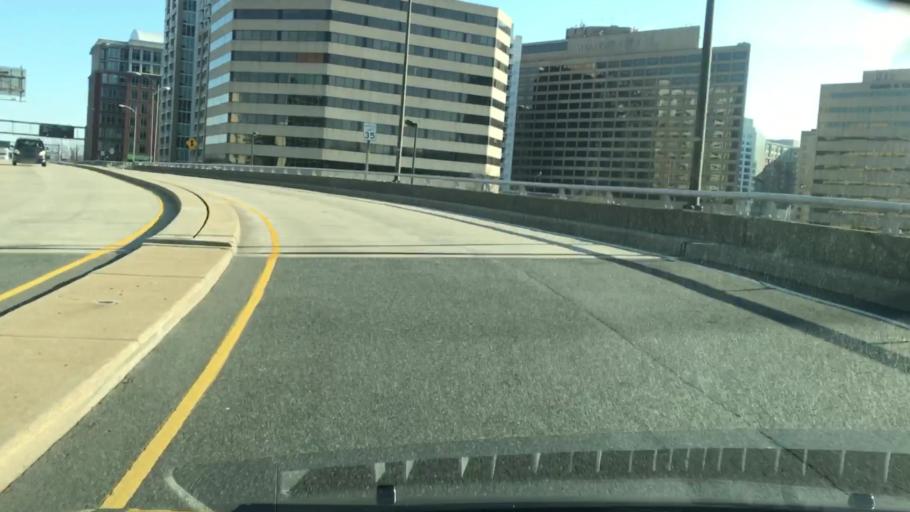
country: US
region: Virginia
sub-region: City of Alexandria
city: Alexandria
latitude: 38.8509
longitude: -77.0532
